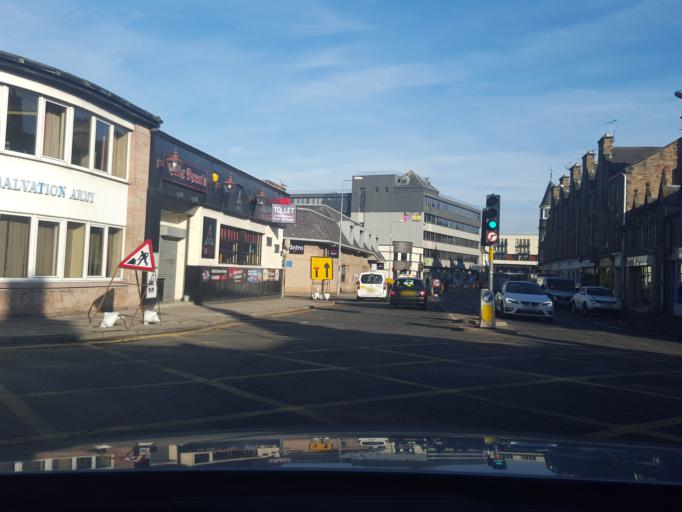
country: GB
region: Scotland
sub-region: Highland
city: Inverness
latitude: 57.4761
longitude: -4.2305
